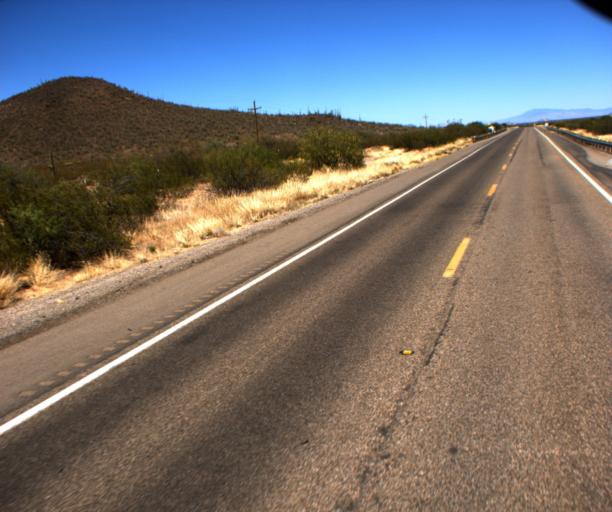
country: US
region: Arizona
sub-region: Pima County
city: Three Points
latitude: 32.0619
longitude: -111.3890
